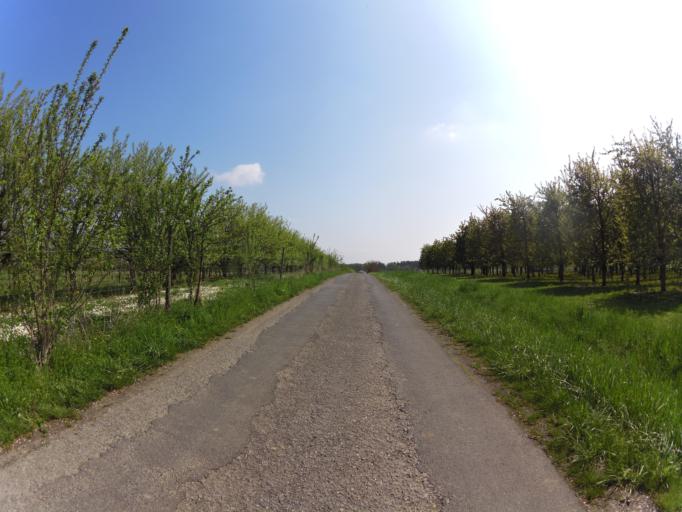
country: DE
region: Bavaria
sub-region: Regierungsbezirk Unterfranken
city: Sommerhausen
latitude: 49.7116
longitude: 10.0508
